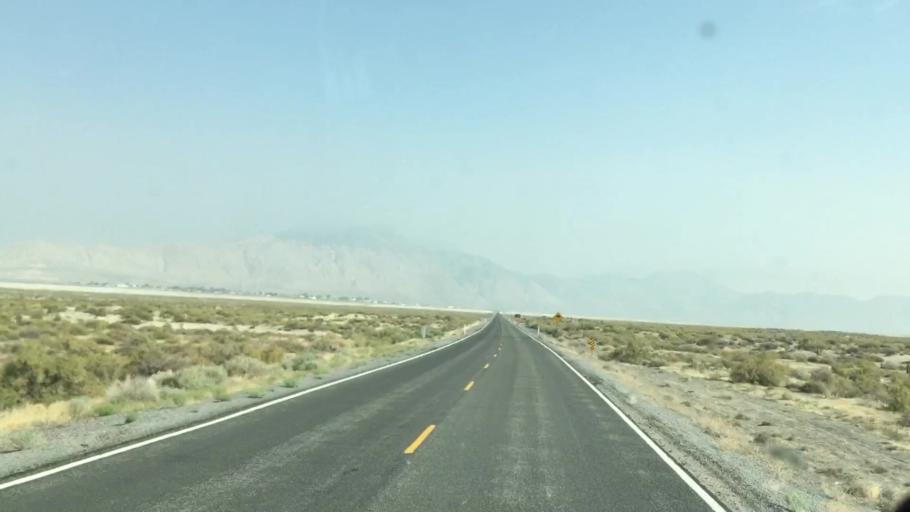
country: US
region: Nevada
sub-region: Pershing County
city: Lovelock
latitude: 40.6232
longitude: -119.3355
